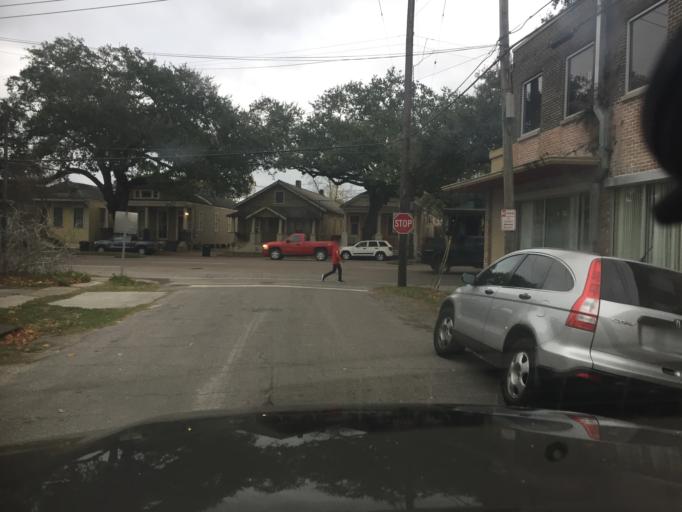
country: US
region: Louisiana
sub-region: Orleans Parish
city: New Orleans
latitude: 29.9814
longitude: -90.0777
